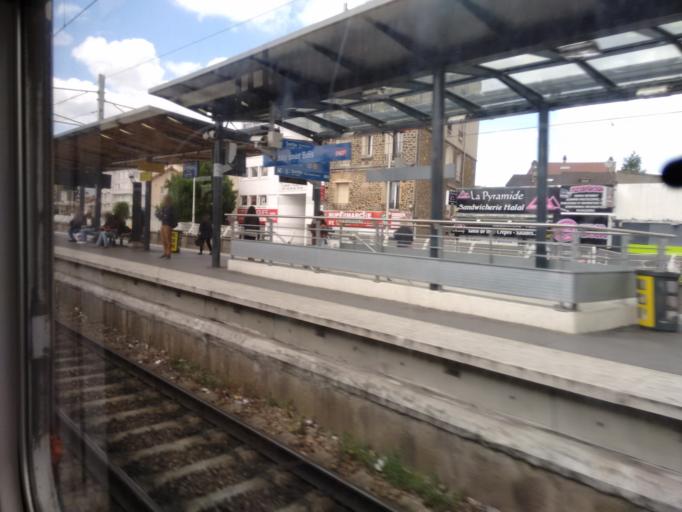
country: FR
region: Ile-de-France
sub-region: Departement de Seine-Saint-Denis
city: Aulnay-sous-Bois
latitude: 48.9322
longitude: 2.4947
